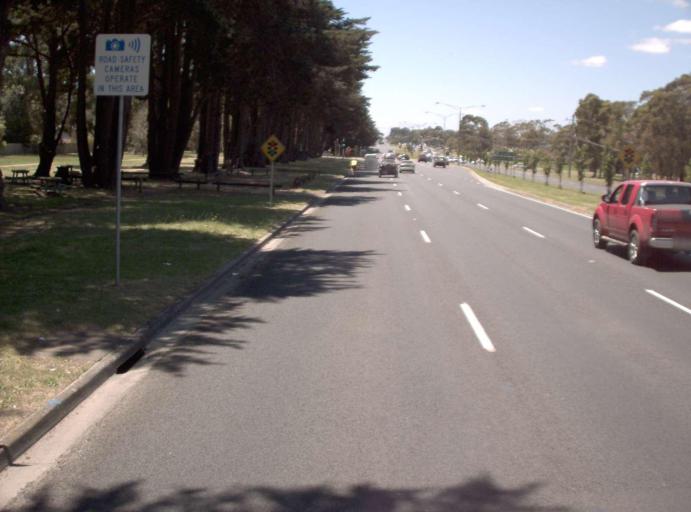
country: AU
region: Victoria
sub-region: Mornington Peninsula
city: Mornington
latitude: -38.2218
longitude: 145.0546
